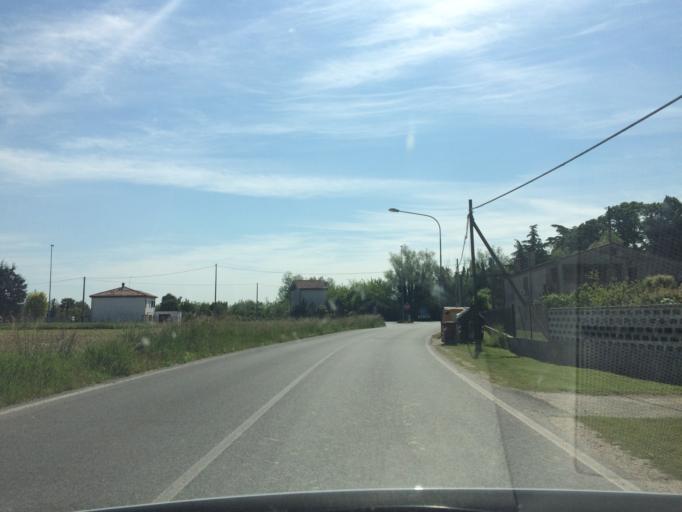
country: IT
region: Veneto
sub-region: Provincia di Padova
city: Abano Terme
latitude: 45.3500
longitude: 11.8027
